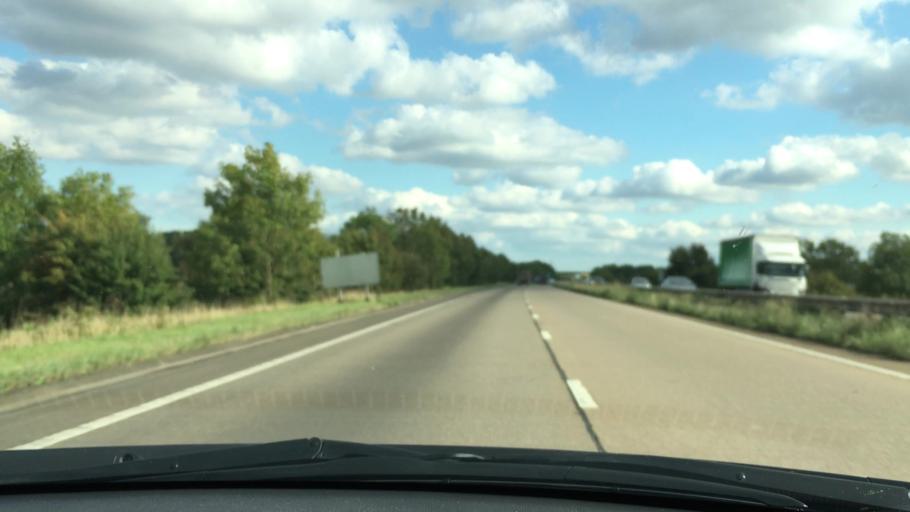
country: GB
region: England
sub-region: North East Lincolnshire
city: Healing
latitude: 53.5915
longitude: -0.1646
